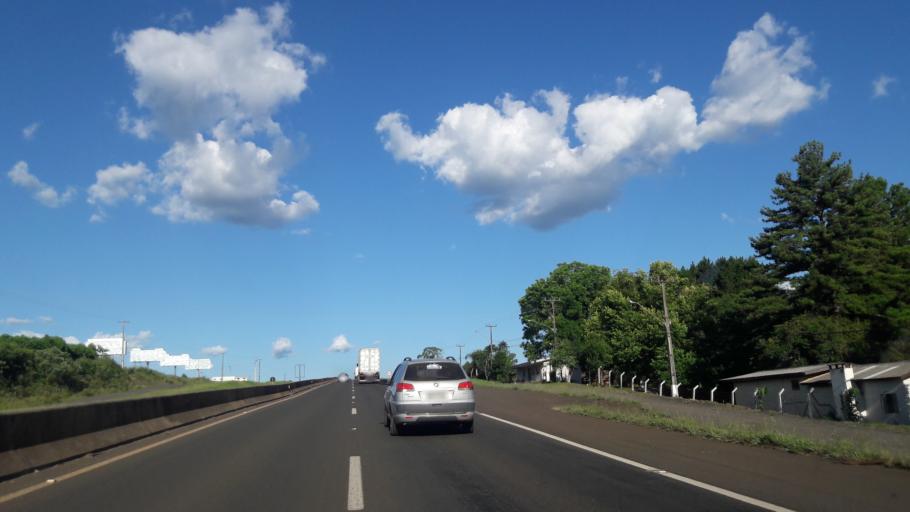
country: BR
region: Parana
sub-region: Guarapuava
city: Guarapuava
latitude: -25.3472
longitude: -51.4505
